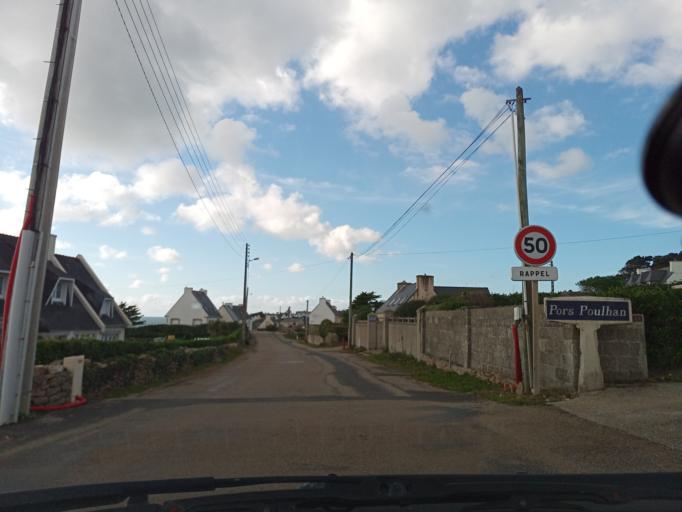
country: FR
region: Brittany
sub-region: Departement du Finistere
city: Plozevet
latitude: 47.9832
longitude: -4.4556
